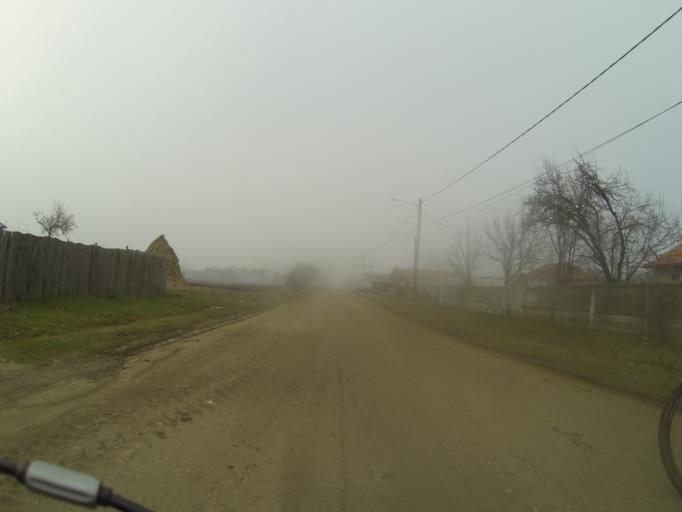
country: RO
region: Mehedinti
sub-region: Comuna Baclesu
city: Baclesu
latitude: 44.4802
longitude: 23.1075
